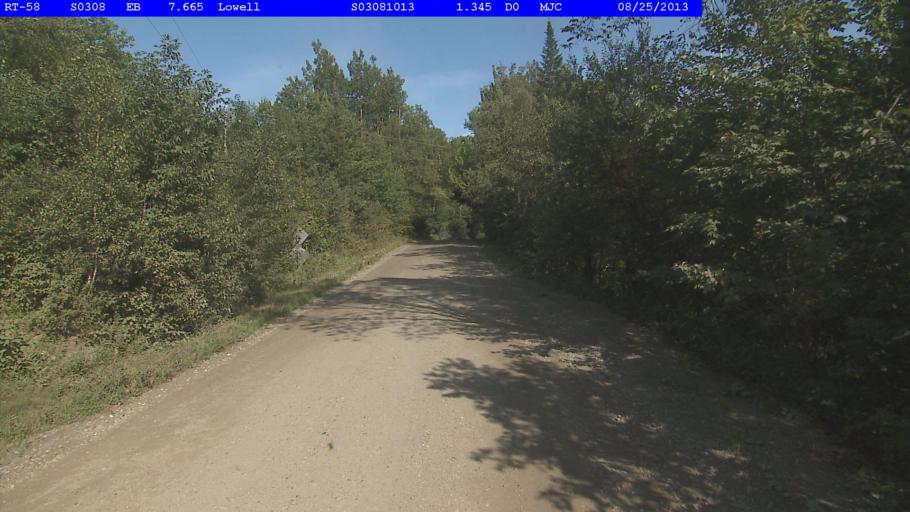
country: US
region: Vermont
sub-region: Franklin County
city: Richford
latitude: 44.8242
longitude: -72.4869
